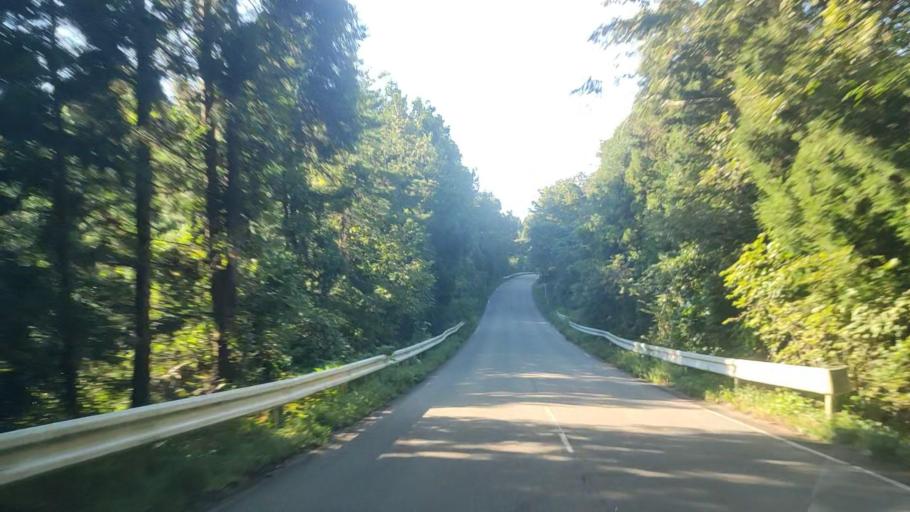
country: JP
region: Ishikawa
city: Nanao
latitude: 37.1199
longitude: 136.9378
